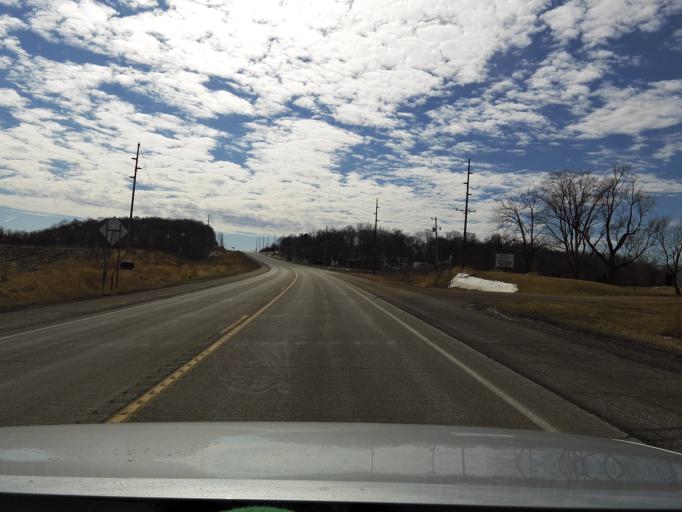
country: US
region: Minnesota
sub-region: Le Sueur County
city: New Prague
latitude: 44.5355
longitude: -93.5855
